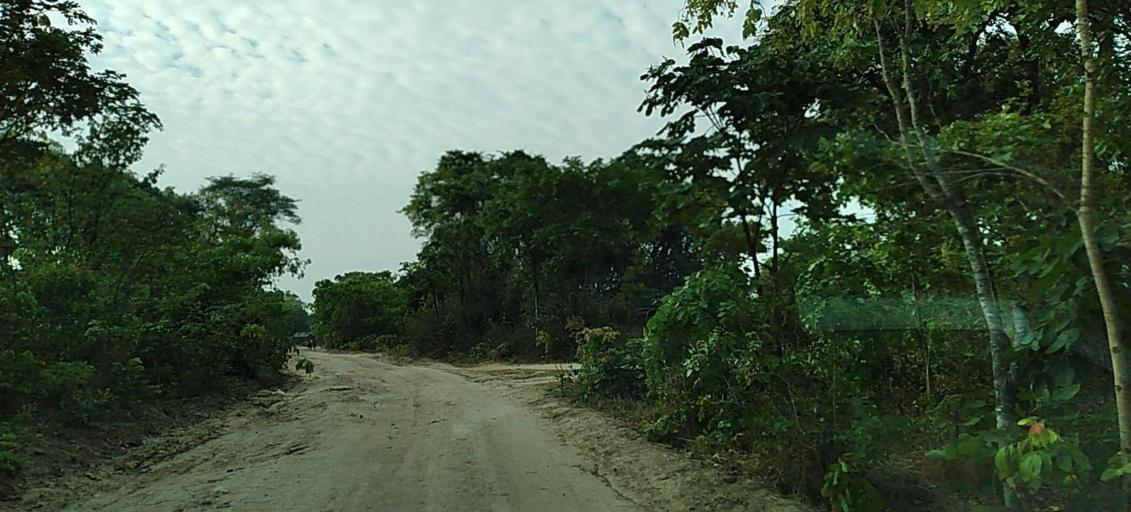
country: ZM
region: Copperbelt
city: Kalulushi
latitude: -12.8983
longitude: 27.6856
